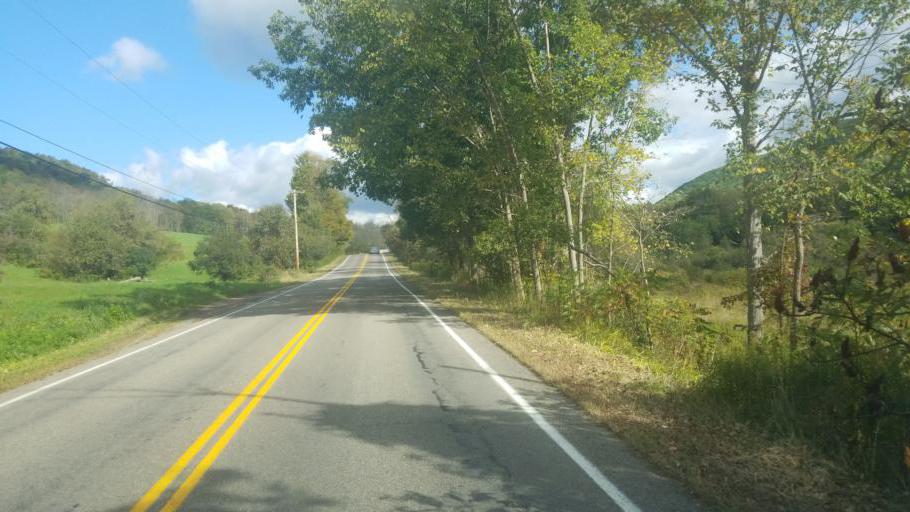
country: US
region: New York
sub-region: Allegany County
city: Cuba
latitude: 42.2220
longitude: -78.3114
